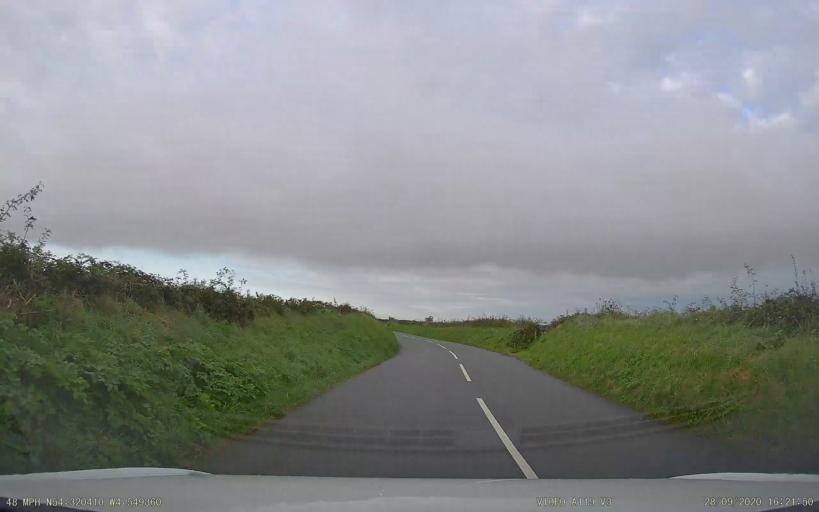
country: IM
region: Ramsey
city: Ramsey
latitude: 54.3204
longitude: -4.5494
